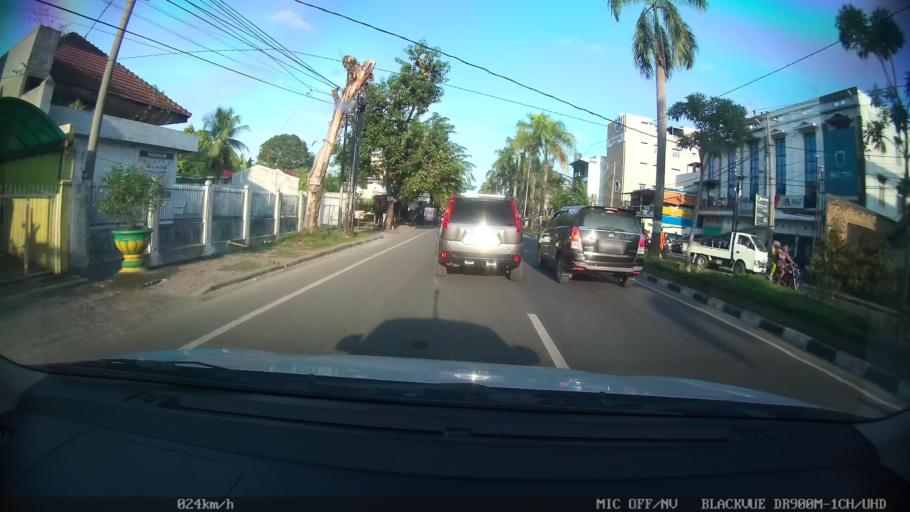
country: ID
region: North Sumatra
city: Medan
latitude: 3.6072
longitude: 98.6663
